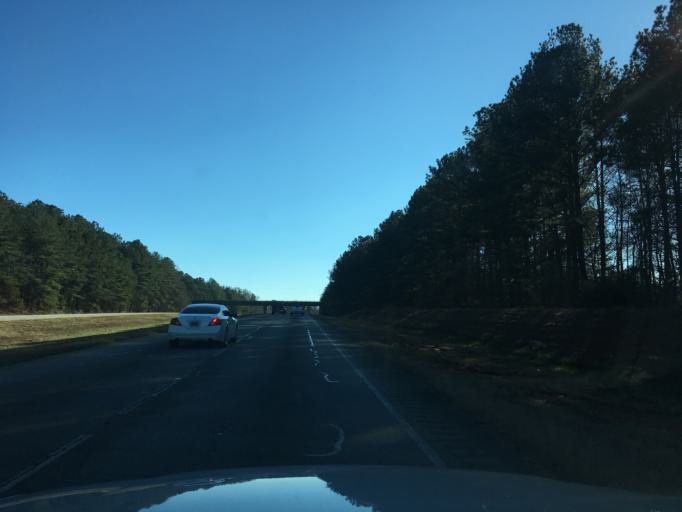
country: US
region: Georgia
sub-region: Carroll County
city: Carrollton
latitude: 33.5798
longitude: -85.0418
